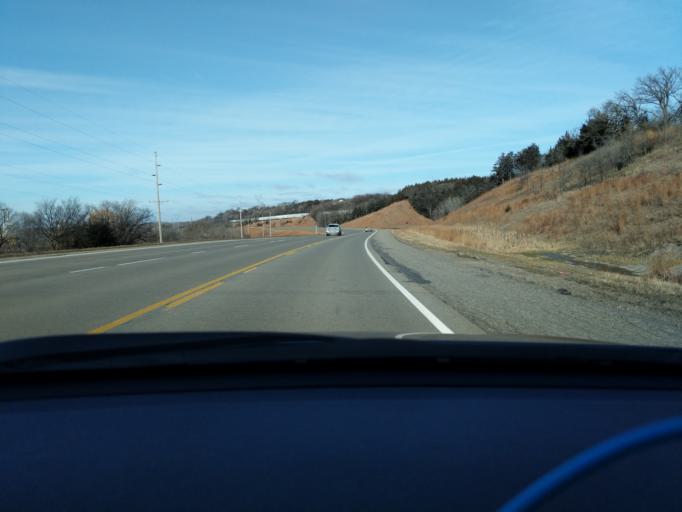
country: US
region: Minnesota
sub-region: Yellow Medicine County
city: Granite Falls
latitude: 44.7986
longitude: -95.5081
